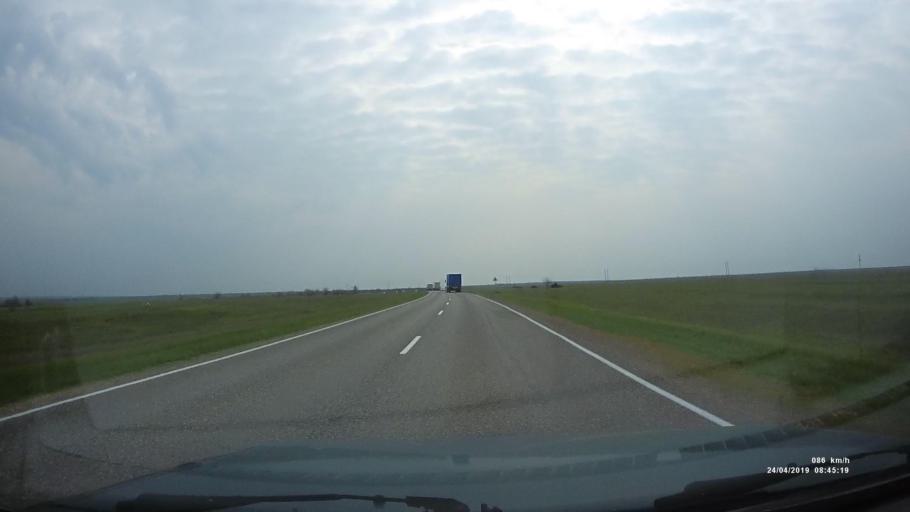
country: RU
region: Kalmykiya
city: Arshan'
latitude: 46.2364
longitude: 44.0588
